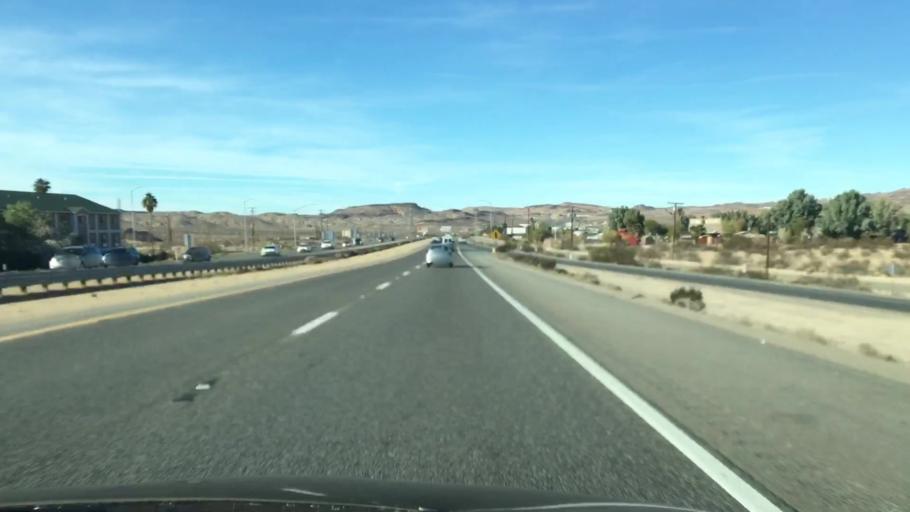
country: US
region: California
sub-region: San Bernardino County
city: Barstow
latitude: 34.9023
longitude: -116.8888
